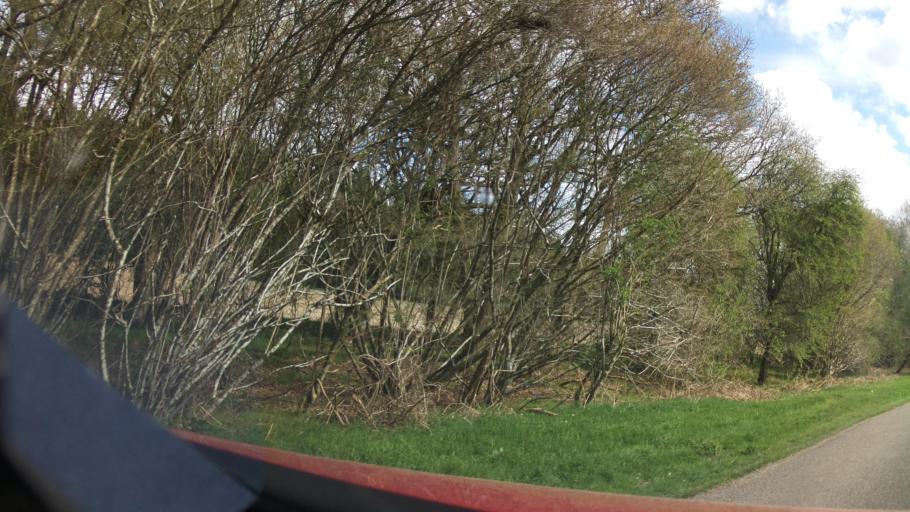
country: GB
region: England
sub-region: Hampshire
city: Highclere
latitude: 51.3045
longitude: -1.4562
